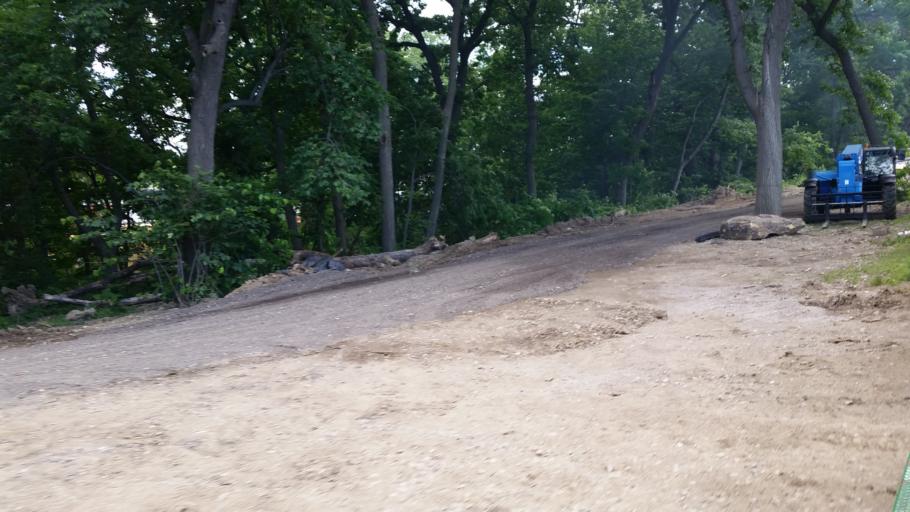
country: US
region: Nebraska
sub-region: Douglas County
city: Omaha
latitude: 41.2235
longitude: -95.9245
